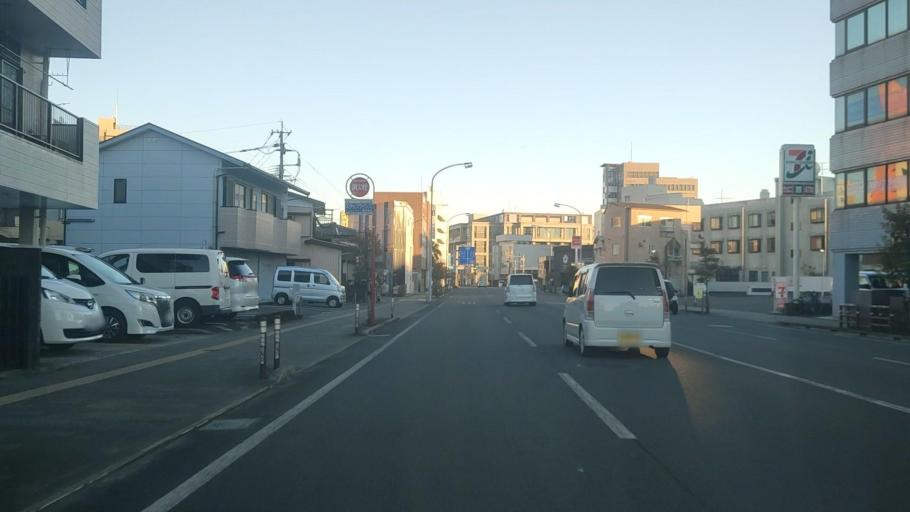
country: JP
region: Miyazaki
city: Miyazaki-shi
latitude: 31.9101
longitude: 131.4175
